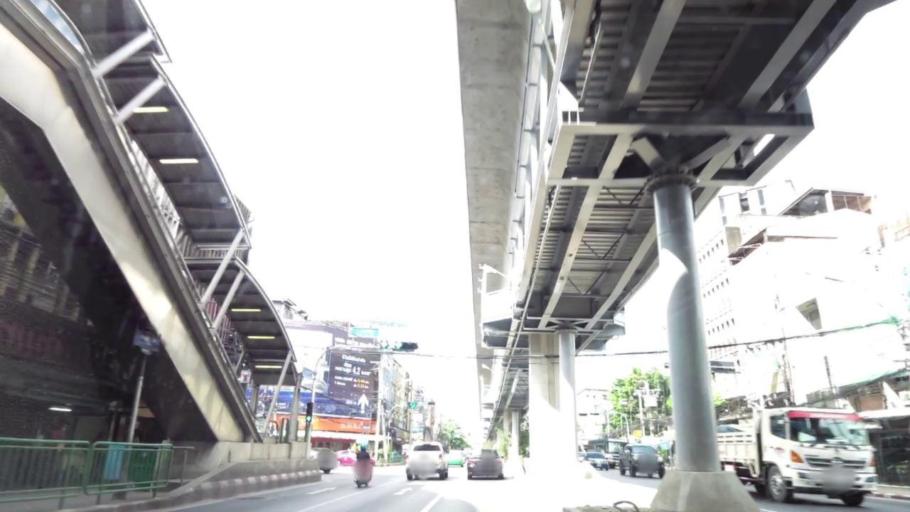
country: TH
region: Bangkok
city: Phra Khanong
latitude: 13.6794
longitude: 100.6094
